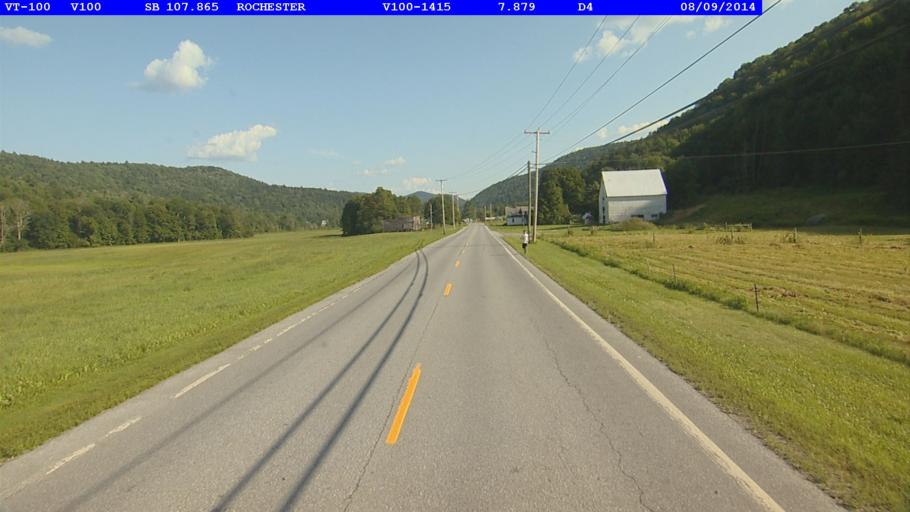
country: US
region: Vermont
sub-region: Orange County
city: Randolph
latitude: 43.9064
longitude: -72.8290
